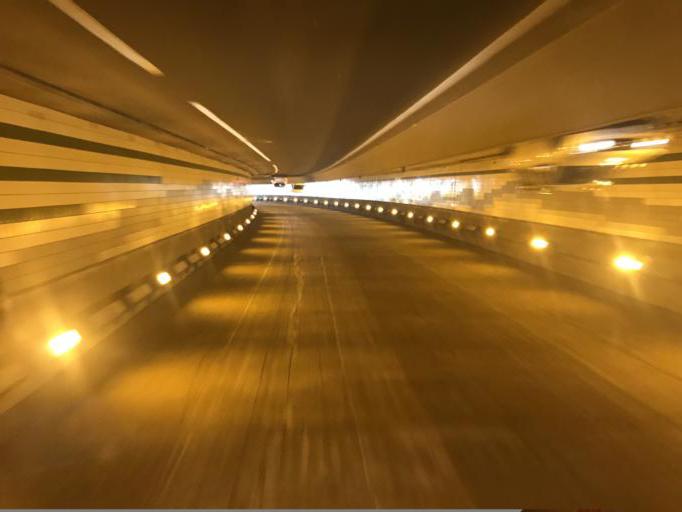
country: FR
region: Limousin
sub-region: Departement de la Correze
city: Tulle
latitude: 45.2508
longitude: 1.7631
